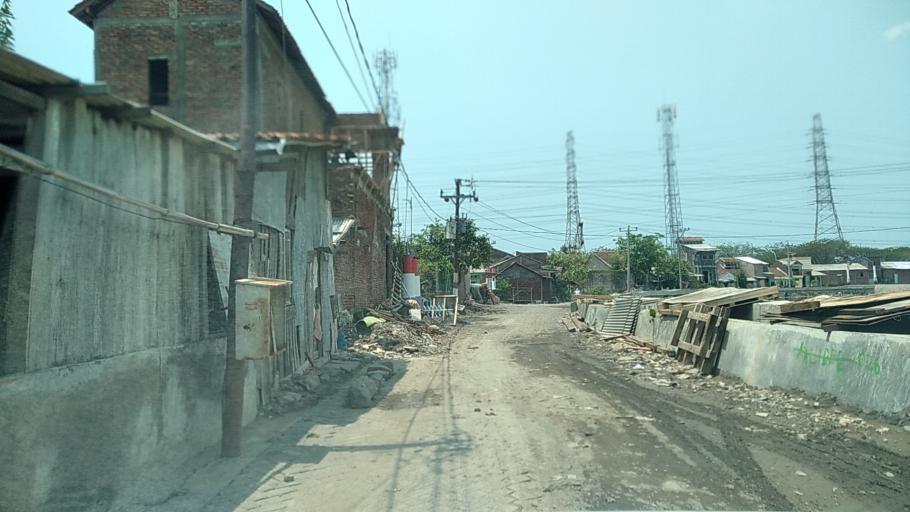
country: ID
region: Central Java
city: Semarang
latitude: -6.9534
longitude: 110.4374
